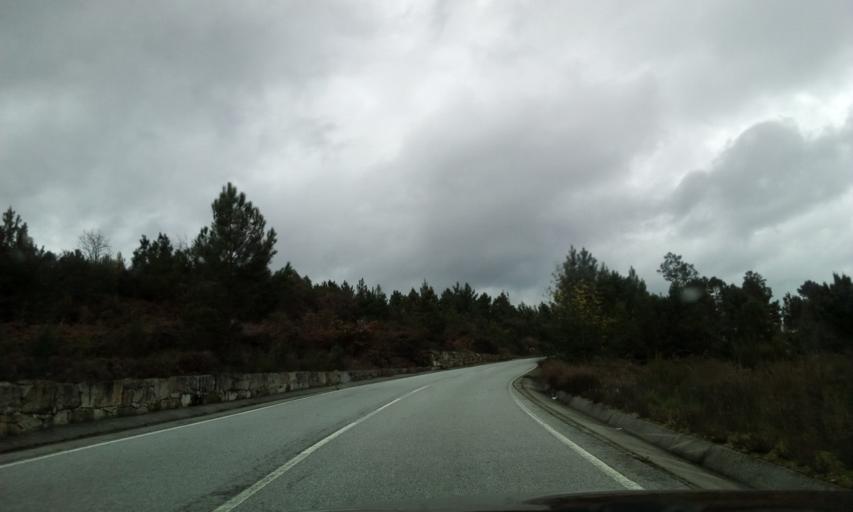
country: PT
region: Viseu
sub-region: Viseu
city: Rio de Loba
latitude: 40.6165
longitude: -7.8651
